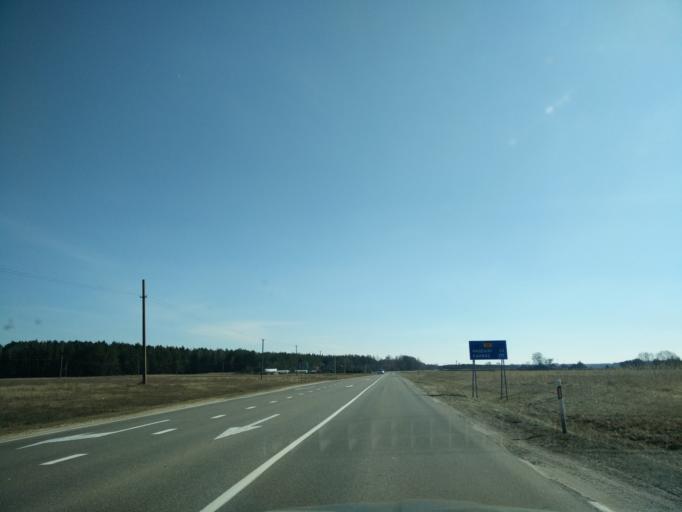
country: LT
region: Klaipedos apskritis
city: Silute
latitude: 55.3313
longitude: 21.5159
